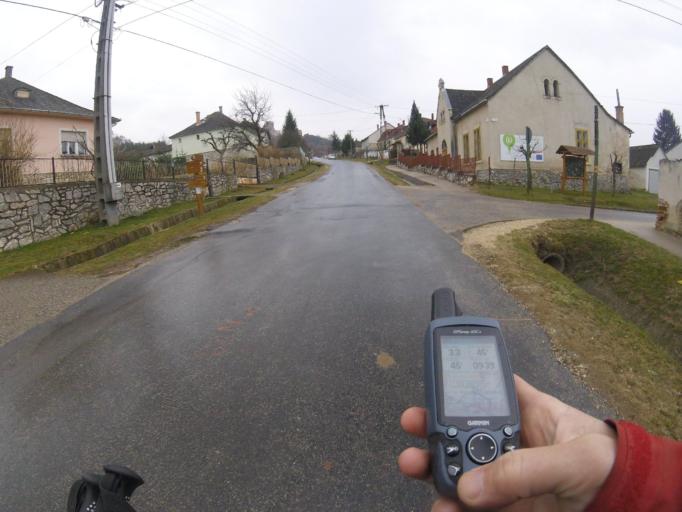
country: HU
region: Gyor-Moson-Sopron
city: Bakonyszentlaszlo
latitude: 47.3555
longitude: 17.8817
